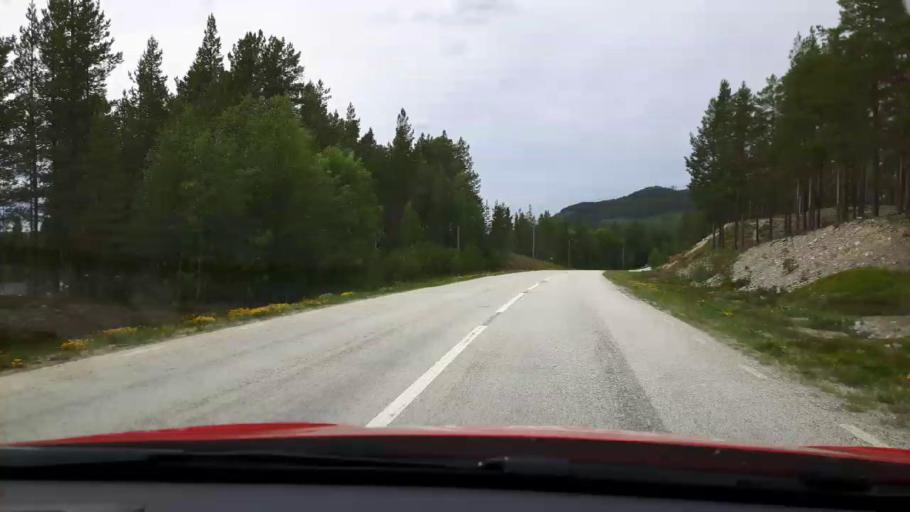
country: SE
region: Jaemtland
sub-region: Harjedalens Kommun
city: Sveg
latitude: 62.4114
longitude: 13.6454
